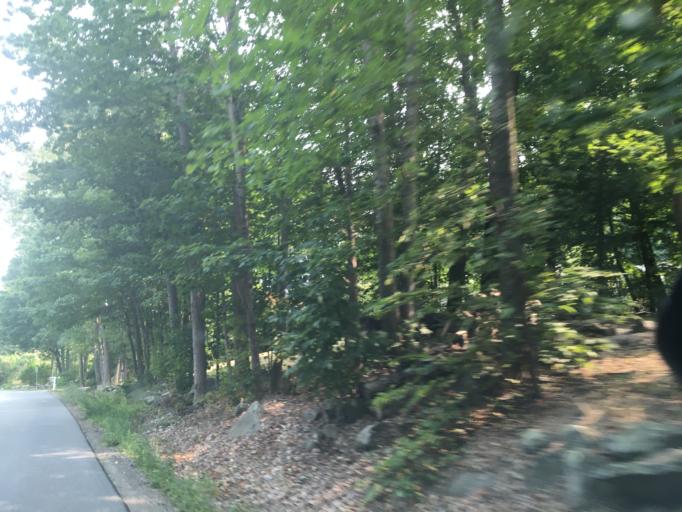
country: US
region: New Hampshire
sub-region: Rockingham County
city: Exeter
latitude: 42.9894
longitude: -70.8935
